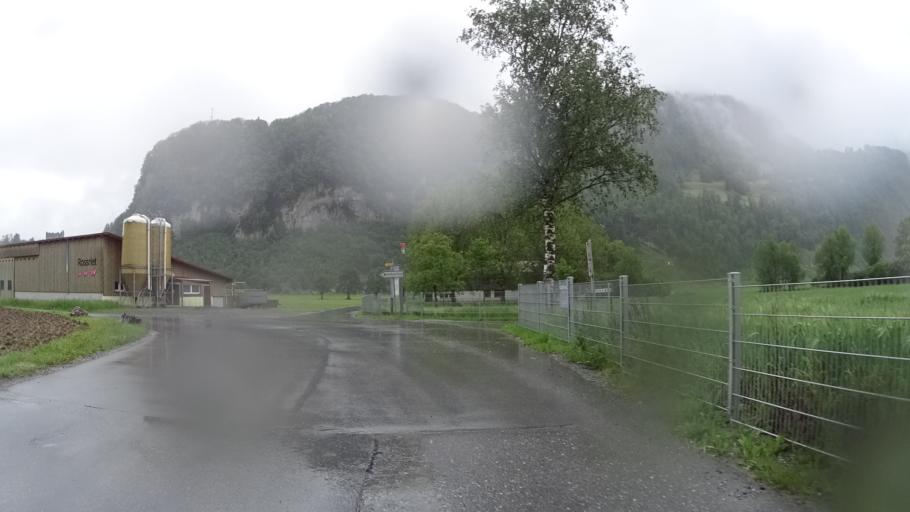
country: CH
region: Saint Gallen
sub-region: Wahlkreis Sarganserland
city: Walenstadt
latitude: 47.1096
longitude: 9.3290
